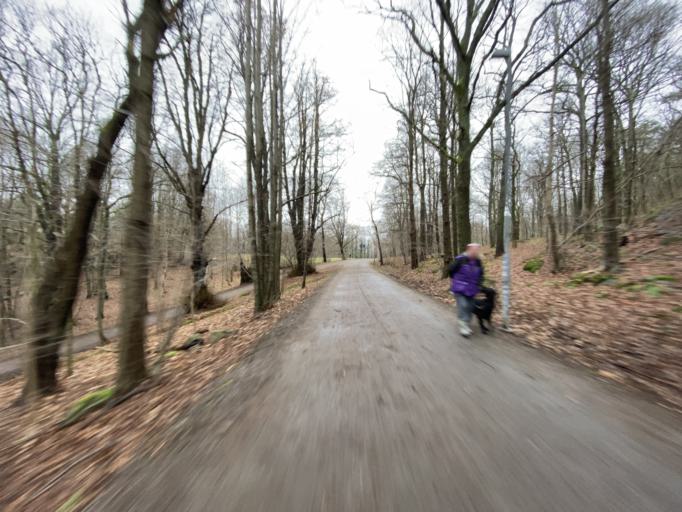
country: SE
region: Vaestra Goetaland
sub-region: Molndal
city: Moelndal
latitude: 57.7077
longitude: 12.0297
